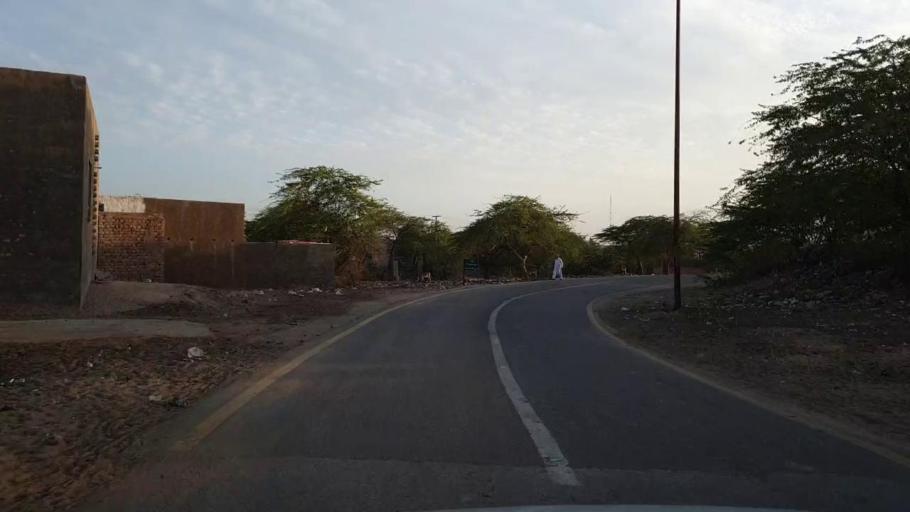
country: PK
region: Sindh
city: Mithi
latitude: 24.9785
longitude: 69.9202
